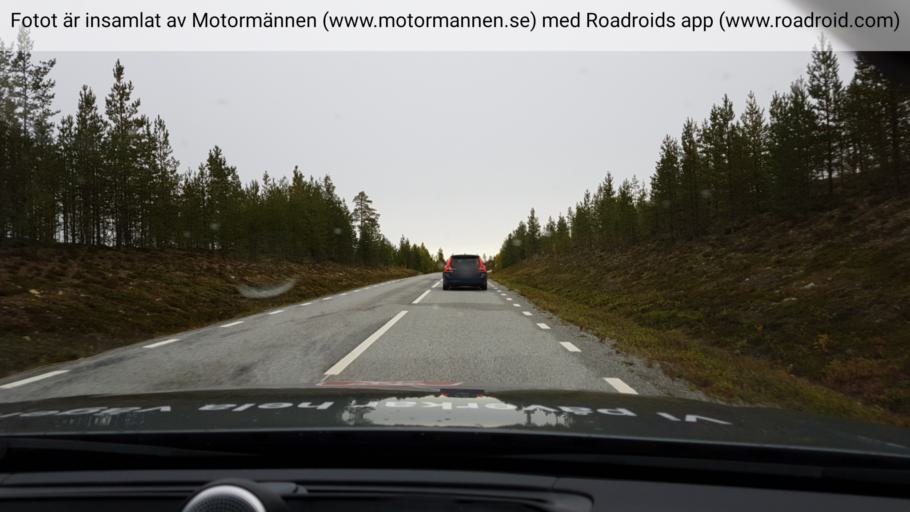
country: SE
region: Jaemtland
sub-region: Stroemsunds Kommun
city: Stroemsund
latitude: 63.9735
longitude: 15.4882
